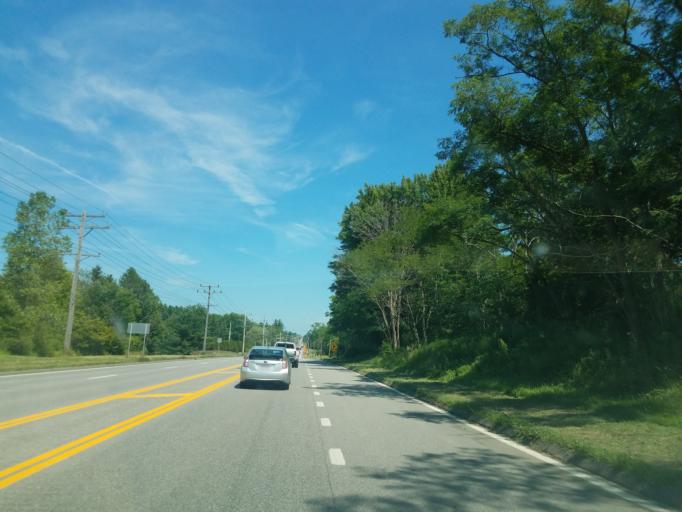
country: US
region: Ohio
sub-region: Cuyahoga County
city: Gates Mills
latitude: 41.5226
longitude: -81.3811
